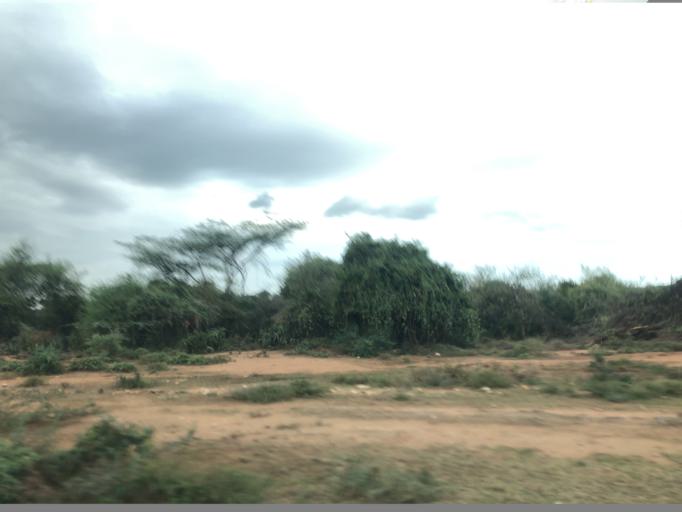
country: ET
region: Southern Nations, Nationalities, and People's Region
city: Turmi
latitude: 5.0752
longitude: 36.5070
